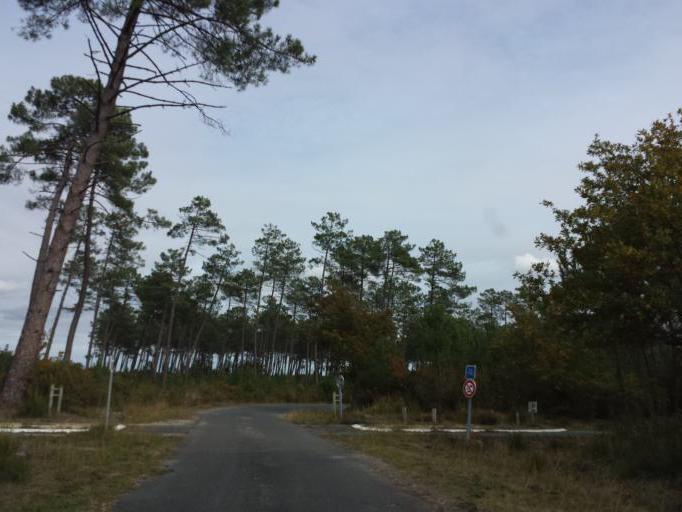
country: FR
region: Aquitaine
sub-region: Departement de la Gironde
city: Lacanau
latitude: 44.9350
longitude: -1.0281
